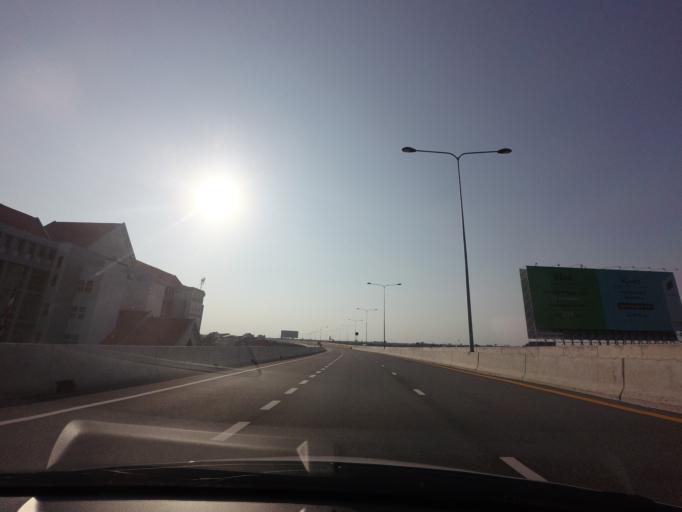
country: TH
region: Bangkok
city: Taling Chan
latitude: 13.7975
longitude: 100.4299
